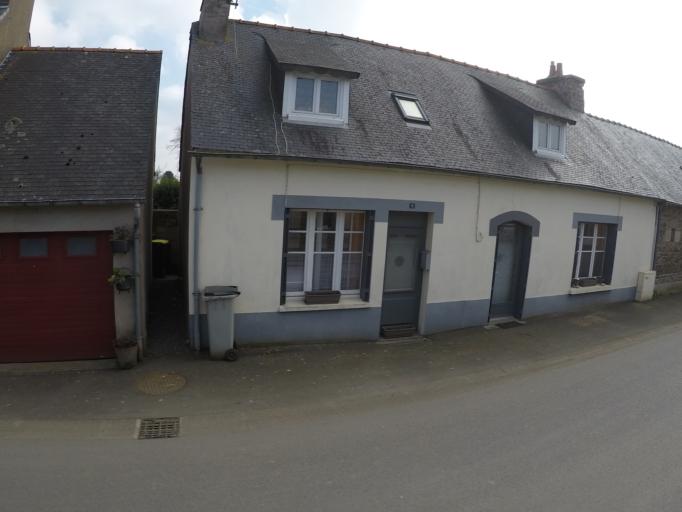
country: FR
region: Brittany
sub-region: Departement des Cotes-d'Armor
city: Pommerit-le-Vicomte
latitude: 48.6186
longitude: -3.0917
